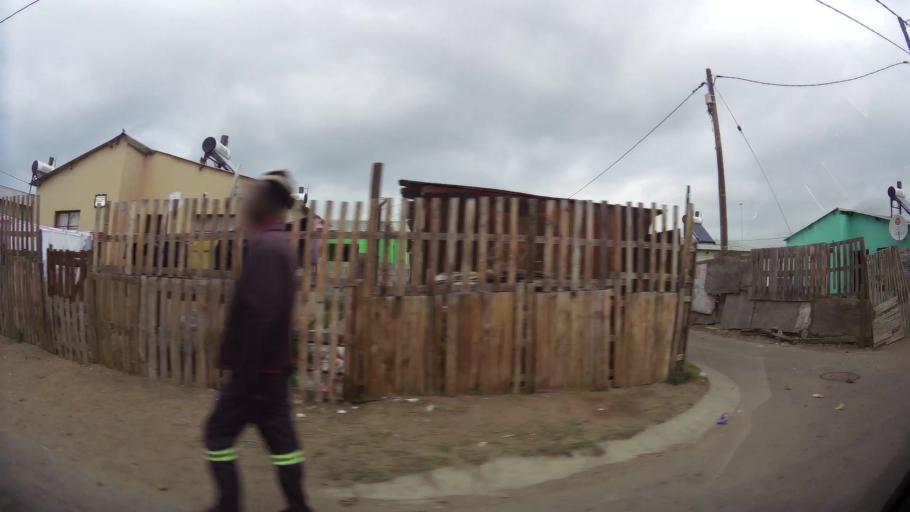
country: ZA
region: Eastern Cape
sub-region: Nelson Mandela Bay Metropolitan Municipality
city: Port Elizabeth
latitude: -33.8887
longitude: 25.5998
